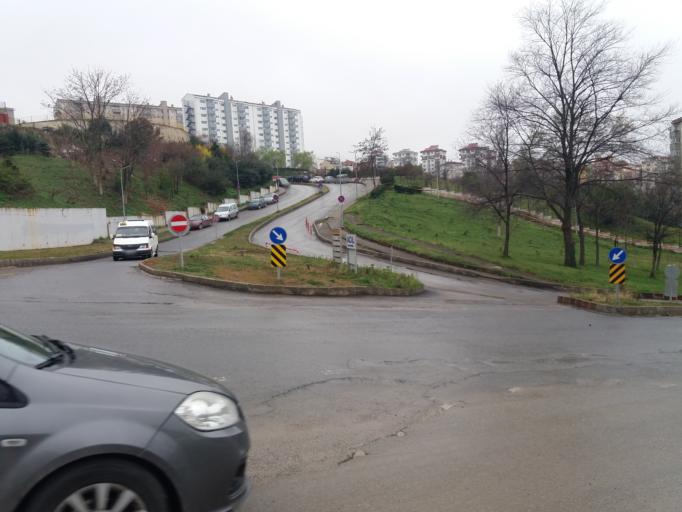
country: TR
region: Trabzon
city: Trabzon
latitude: 40.9941
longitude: 39.7681
